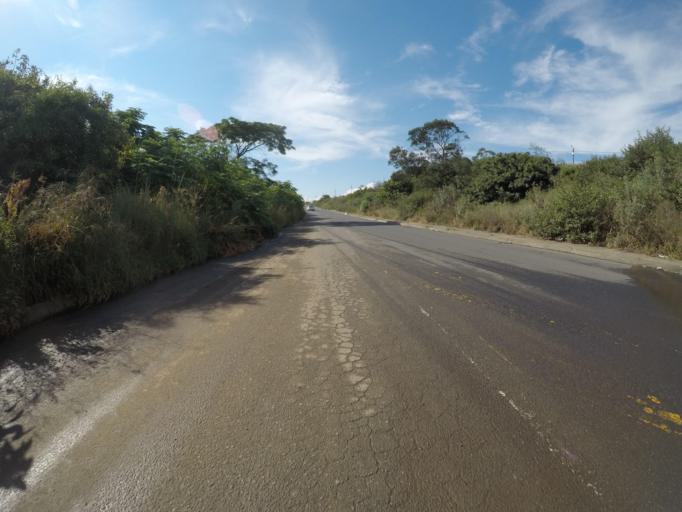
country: ZA
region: Eastern Cape
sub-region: Buffalo City Metropolitan Municipality
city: East London
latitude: -33.0094
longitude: 27.8581
